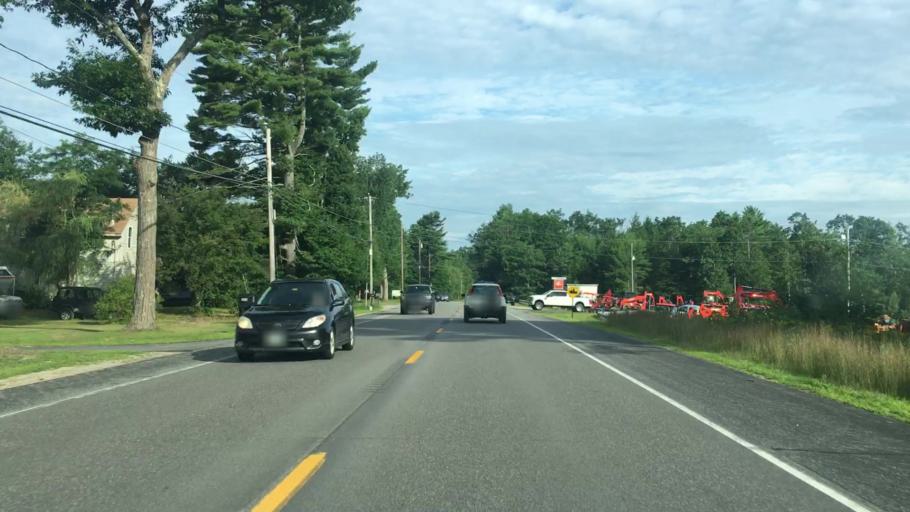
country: US
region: Maine
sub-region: York County
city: Buxton
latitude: 43.7246
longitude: -70.5323
